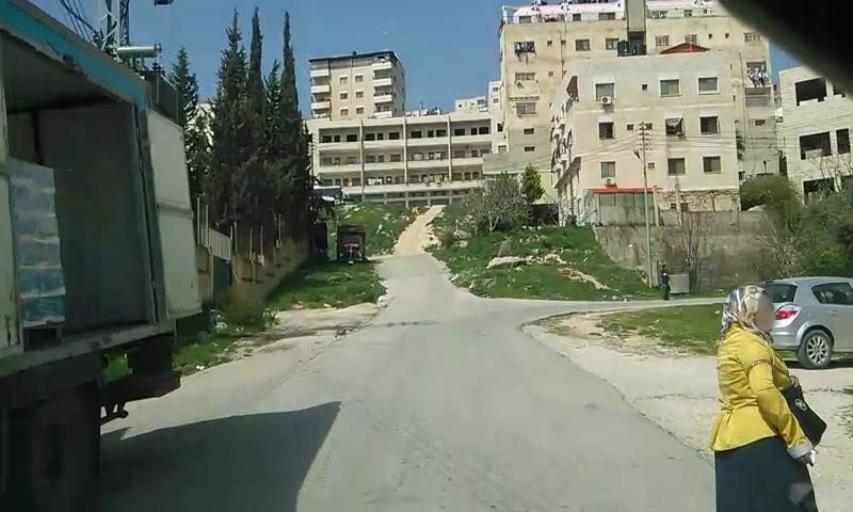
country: PS
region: West Bank
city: `Azmut
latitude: 32.2227
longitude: 35.2964
